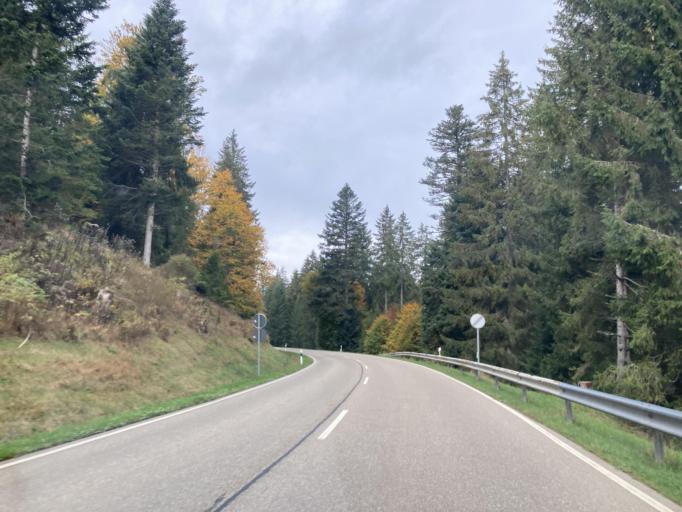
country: DE
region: Baden-Wuerttemberg
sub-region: Karlsruhe Region
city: Biberach
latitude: 48.6558
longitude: 8.2849
